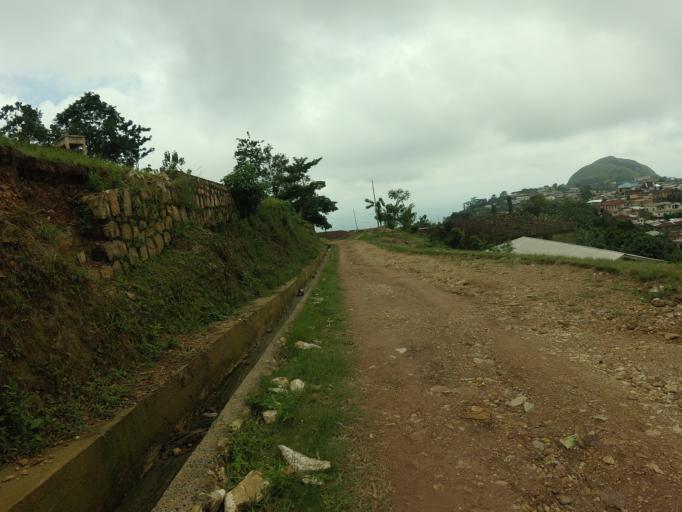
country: TG
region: Plateaux
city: Kpalime
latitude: 6.8436
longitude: 0.4374
